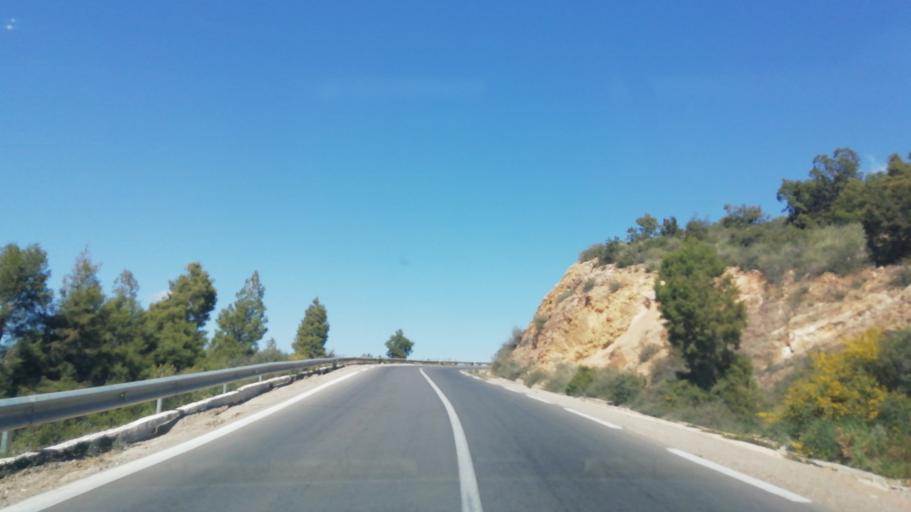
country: DZ
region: Mascara
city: Mascara
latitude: 35.4883
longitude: 0.1471
